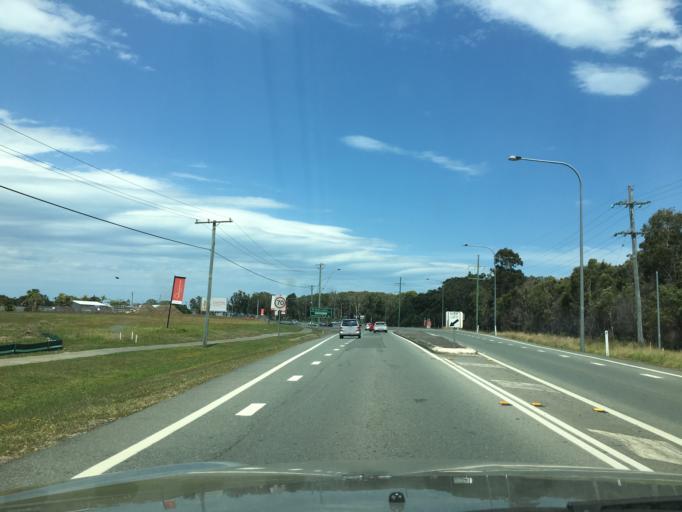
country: AU
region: Queensland
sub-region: Moreton Bay
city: Bongaree
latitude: -27.0730
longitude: 153.1358
